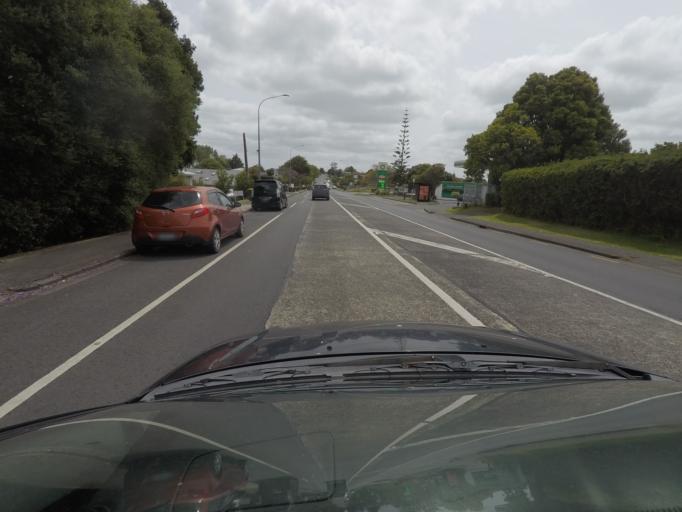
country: NZ
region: Auckland
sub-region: Auckland
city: Pakuranga
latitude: -36.8966
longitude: 174.9218
